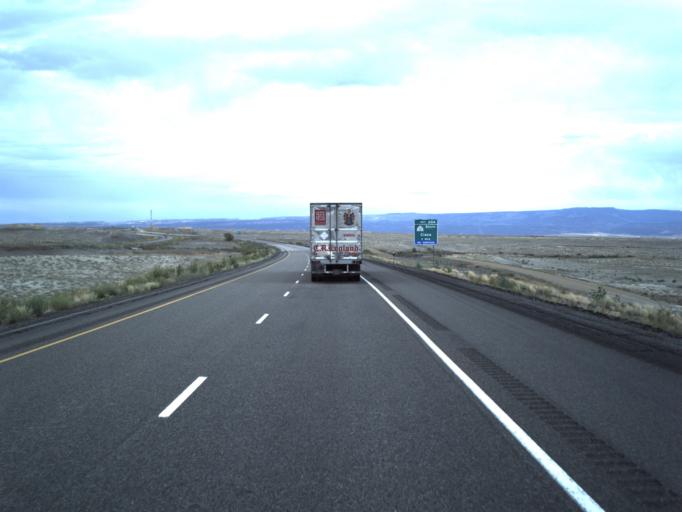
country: US
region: Utah
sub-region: Grand County
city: Moab
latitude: 38.9322
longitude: -109.4304
